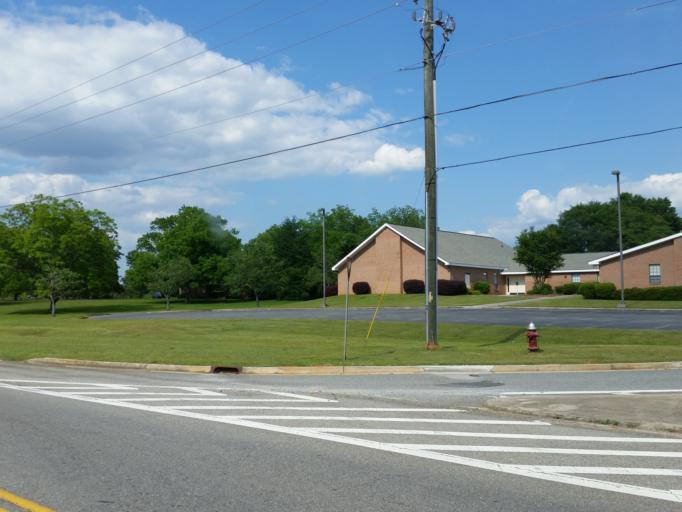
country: US
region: Georgia
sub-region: Houston County
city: Perry
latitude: 32.4900
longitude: -83.7300
